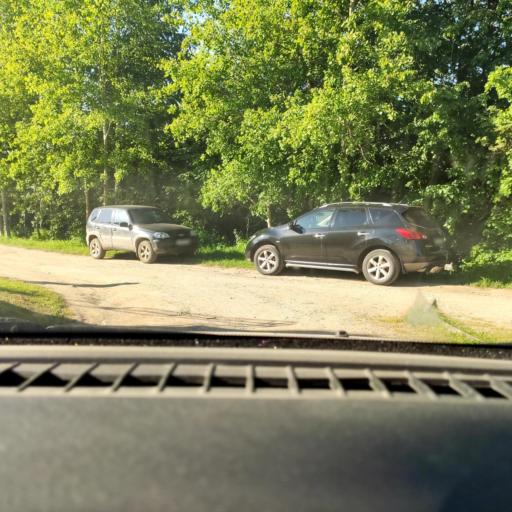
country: RU
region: Perm
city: Overyata
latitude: 58.1196
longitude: 55.8824
